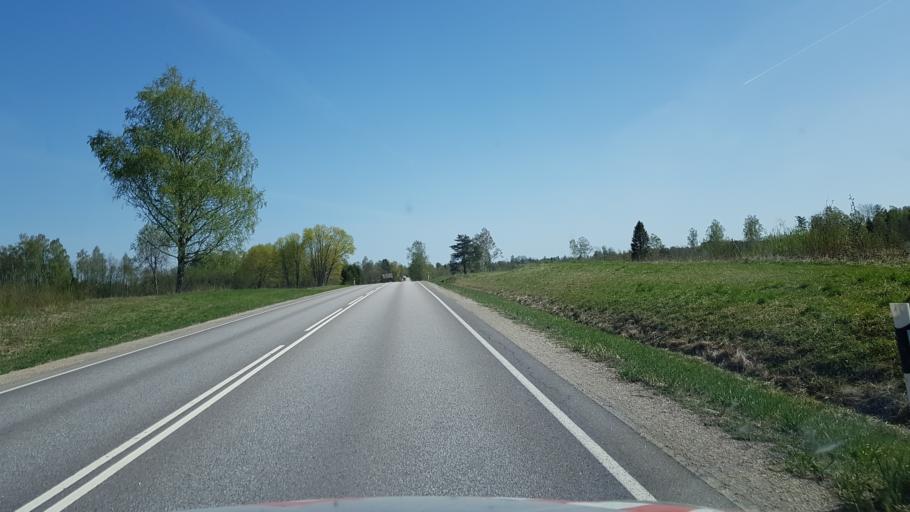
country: EE
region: Valgamaa
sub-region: Torva linn
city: Torva
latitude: 58.0230
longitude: 25.8185
